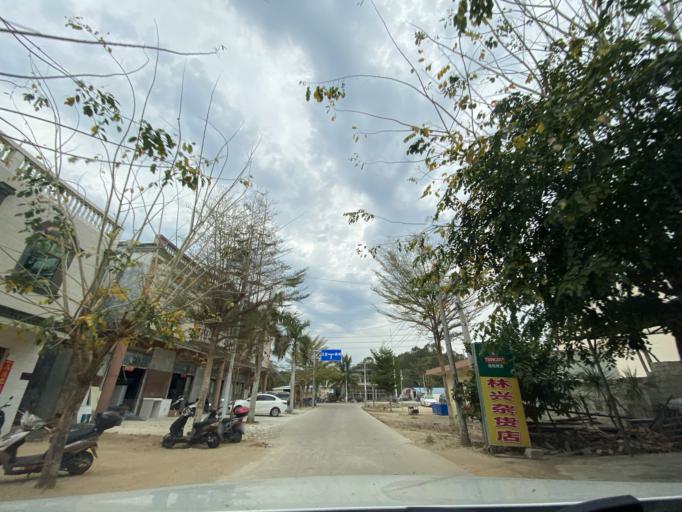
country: CN
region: Hainan
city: Yingzhou
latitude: 18.4229
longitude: 109.8211
